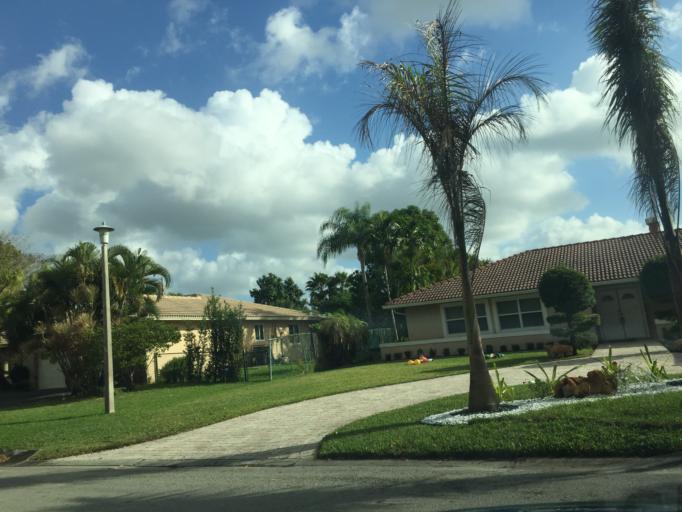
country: US
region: Florida
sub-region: Broward County
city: Tamarac
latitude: 26.2348
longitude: -80.2504
